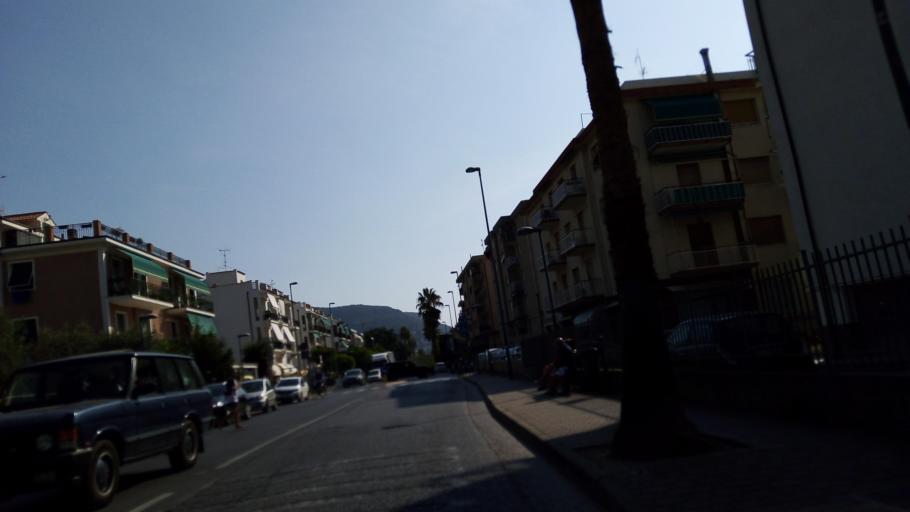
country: IT
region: Liguria
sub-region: Provincia di Savona
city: Pietra Ligure
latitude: 44.1540
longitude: 8.2901
